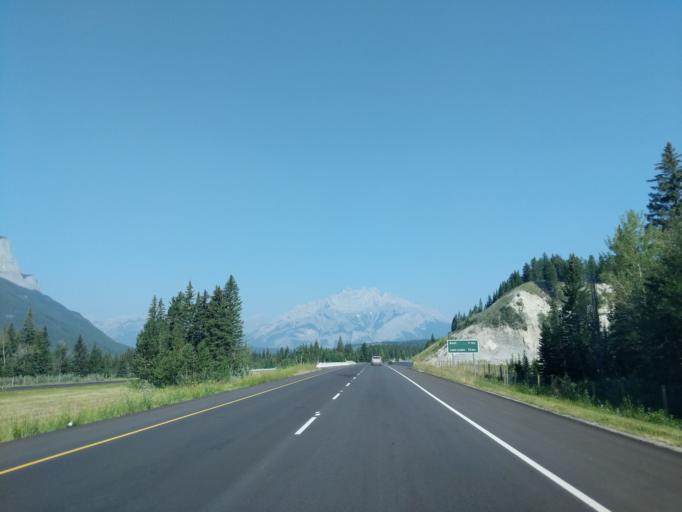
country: CA
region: Alberta
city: Canmore
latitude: 51.1488
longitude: -115.4265
